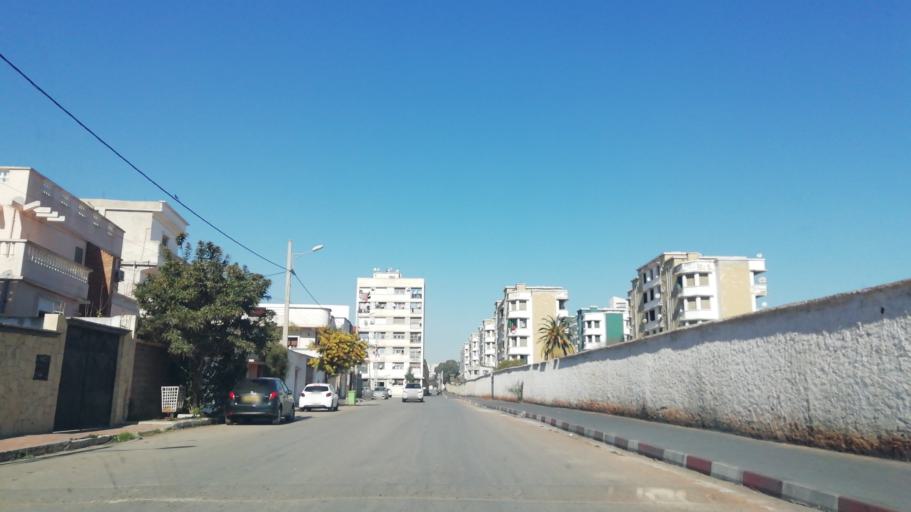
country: DZ
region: Oran
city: Oran
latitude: 35.6756
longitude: -0.6340
